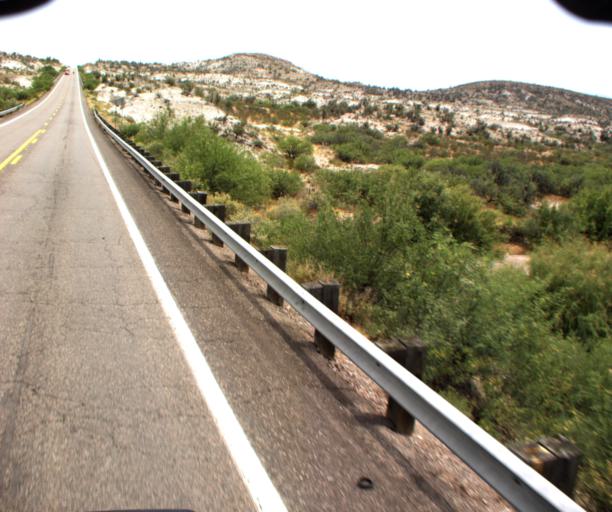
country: US
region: Arizona
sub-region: Graham County
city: Bylas
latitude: 33.2416
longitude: -110.2600
